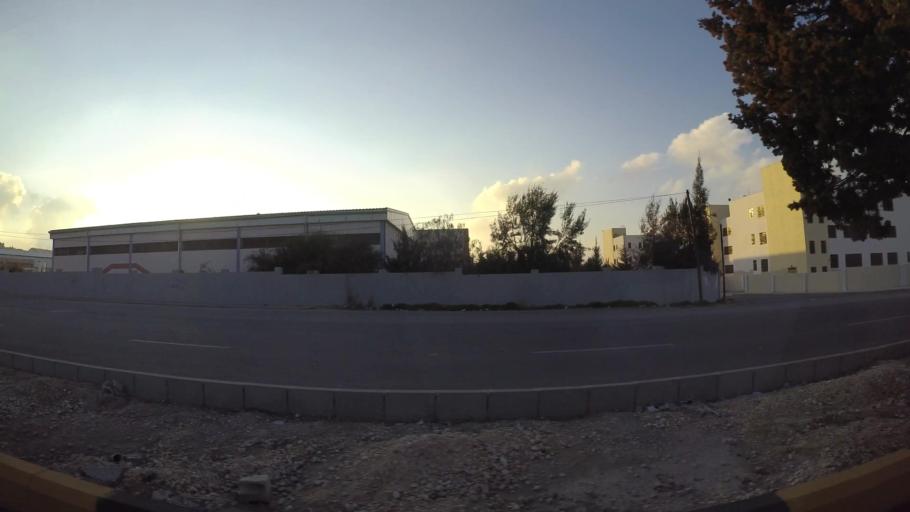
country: JO
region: Amman
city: Al Quwaysimah
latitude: 31.9094
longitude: 35.9228
